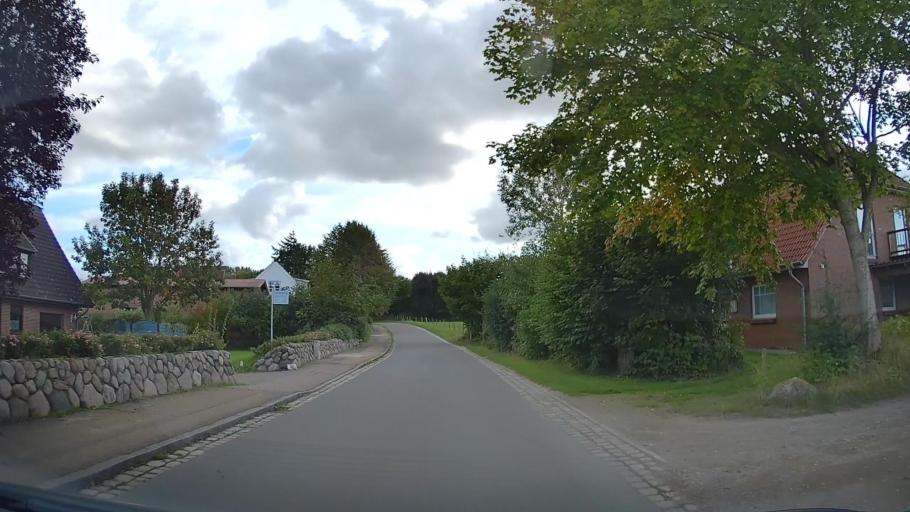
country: DE
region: Schleswig-Holstein
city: Steinberg
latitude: 54.7769
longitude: 9.8000
